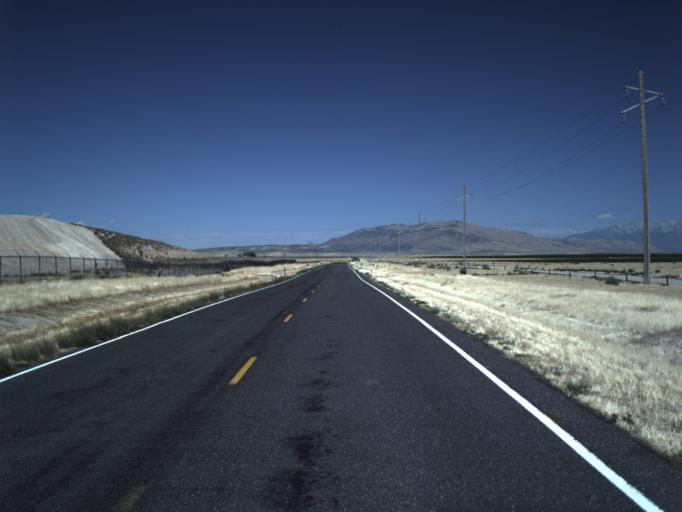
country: US
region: Utah
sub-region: Utah County
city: Genola
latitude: 40.0369
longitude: -111.9584
